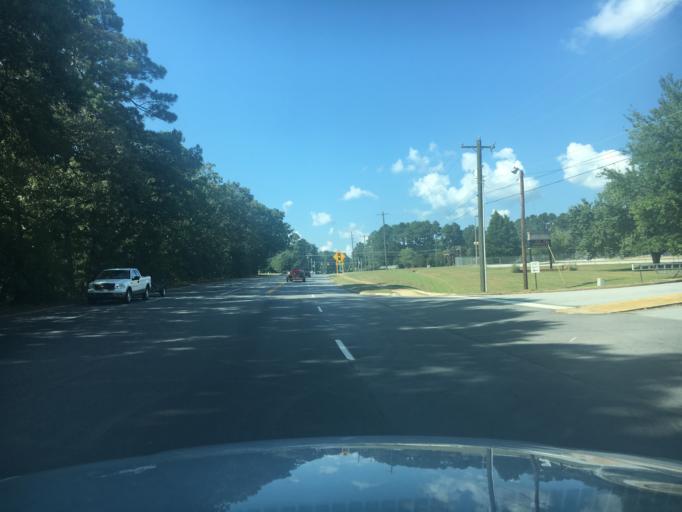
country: US
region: South Carolina
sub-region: Greenwood County
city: Greenwood
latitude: 34.2293
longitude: -82.1768
